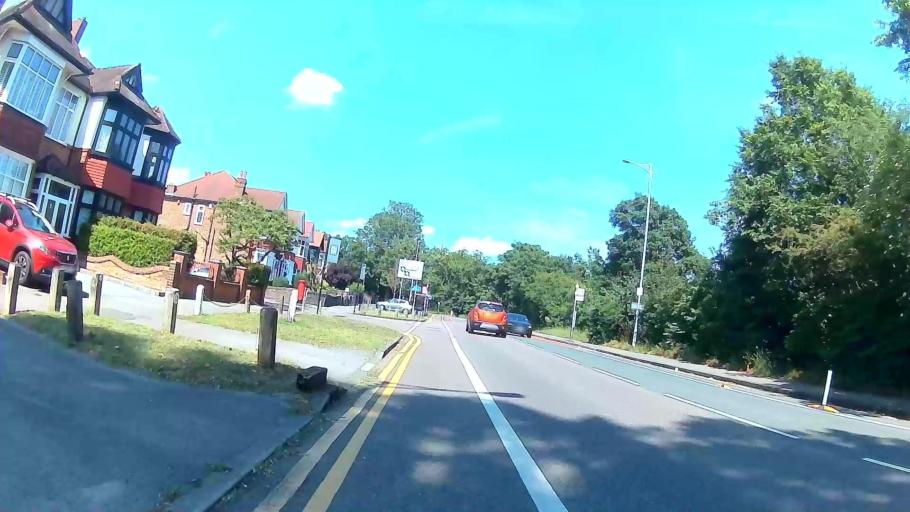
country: GB
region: England
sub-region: Greater London
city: East Ham
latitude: 51.5630
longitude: 0.0239
